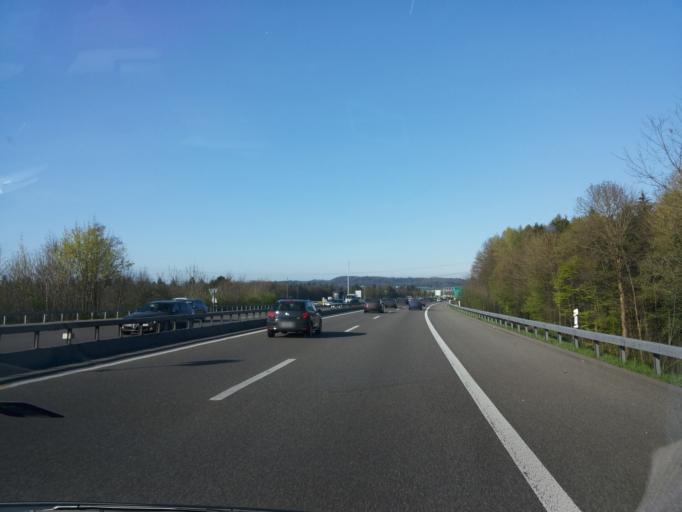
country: CH
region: Aargau
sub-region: Bezirk Lenzburg
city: Othmarsingen
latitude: 47.4194
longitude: 8.2251
